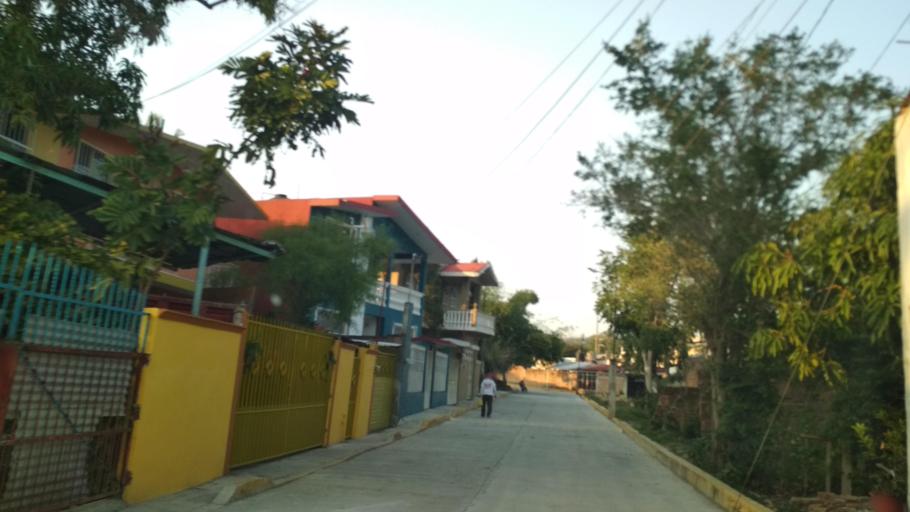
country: MM
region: Shan
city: Taunggyi
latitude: 20.4089
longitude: 97.3367
